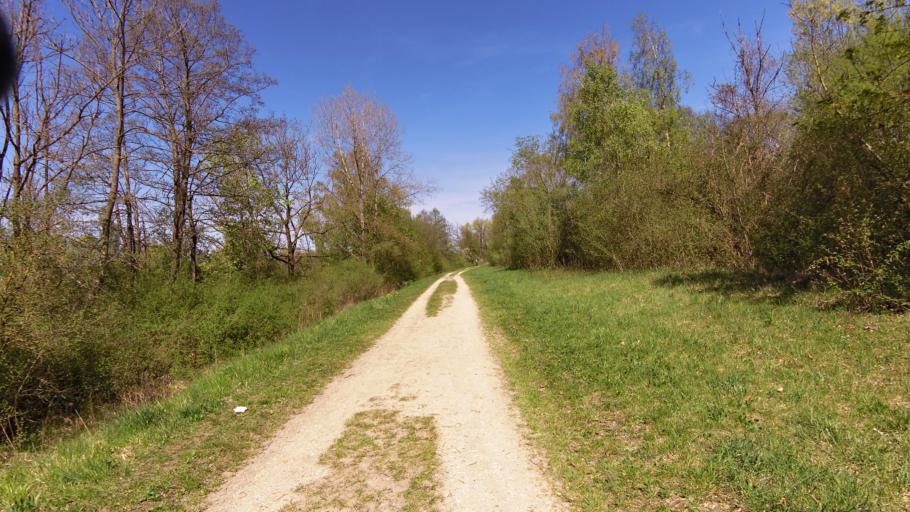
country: DE
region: Bavaria
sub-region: Lower Bavaria
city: Ergolding
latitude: 48.5588
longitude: 12.1827
